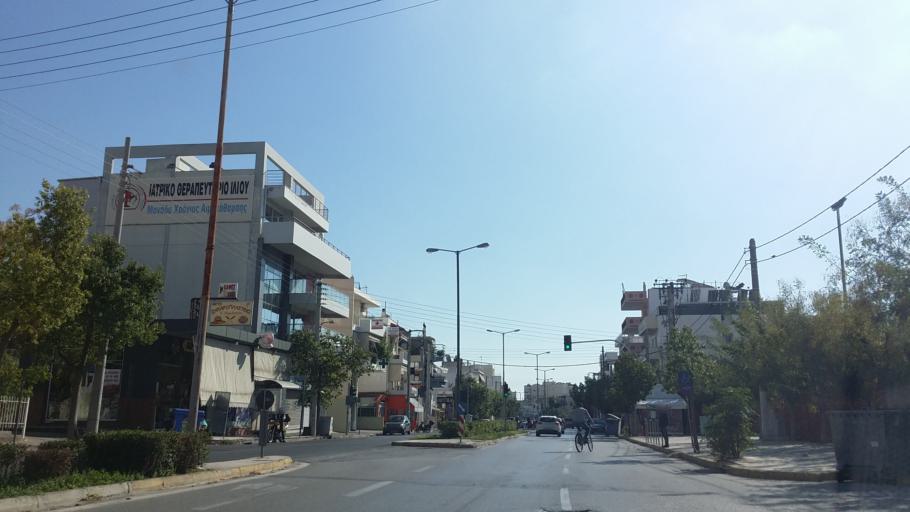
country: GR
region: Attica
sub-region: Nomarchia Athinas
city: Ilion
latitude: 38.0218
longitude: 23.7081
